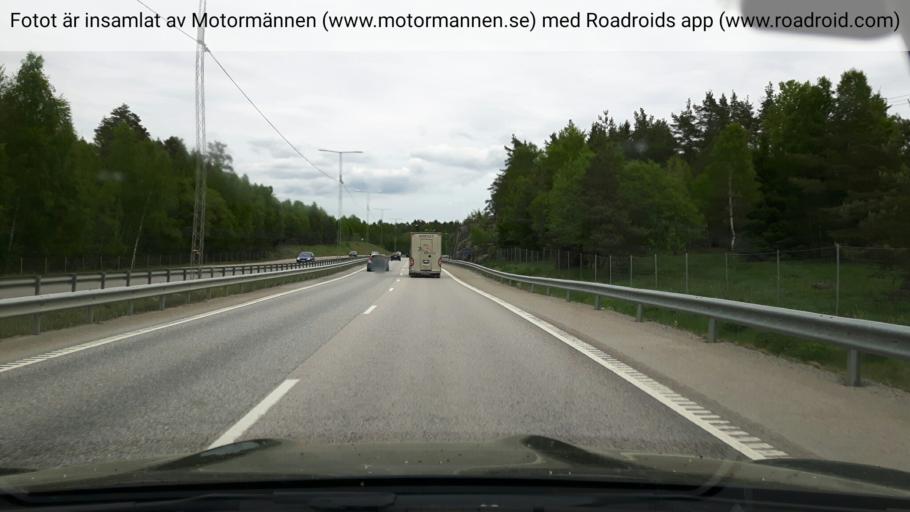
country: SE
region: Stockholm
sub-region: Osterakers Kommun
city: Akersberga
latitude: 59.4945
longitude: 18.2134
